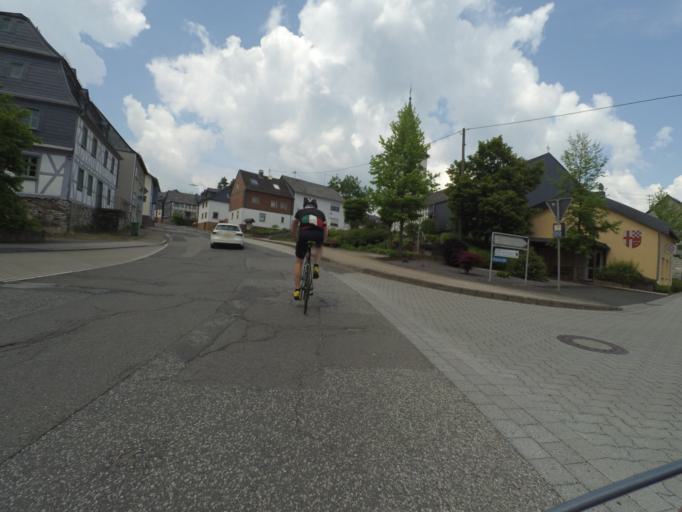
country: DE
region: Rheinland-Pfalz
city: Beltheim
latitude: 50.1058
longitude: 7.4614
